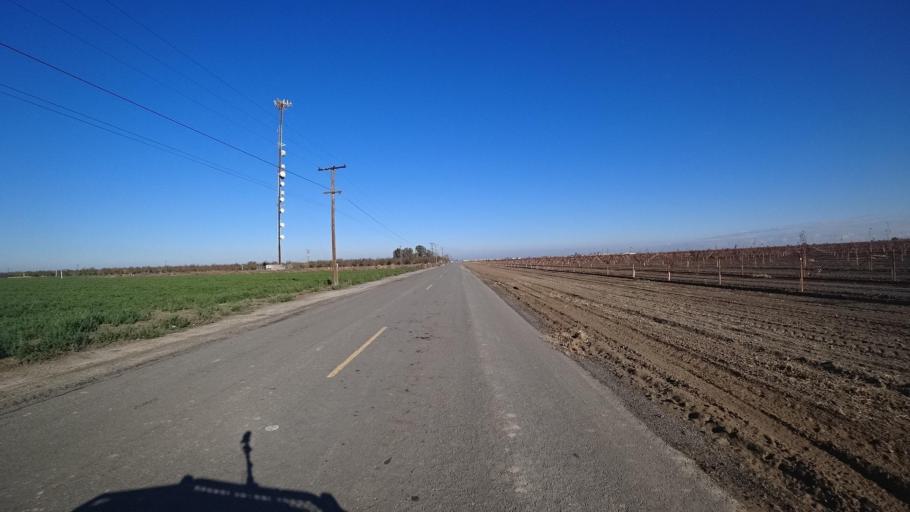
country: US
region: California
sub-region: Kern County
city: Delano
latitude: 35.7517
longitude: -119.3119
